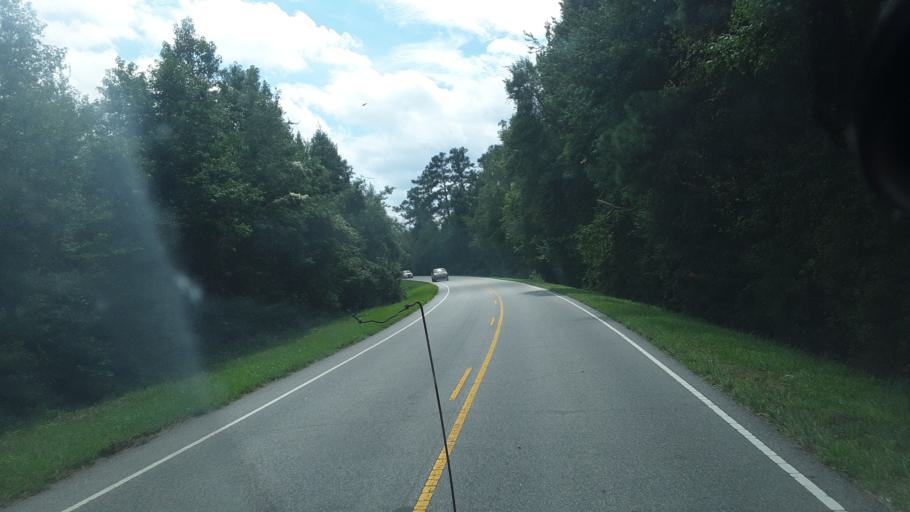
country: US
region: North Carolina
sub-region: Columbus County
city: Tabor City
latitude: 34.2806
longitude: -79.0422
